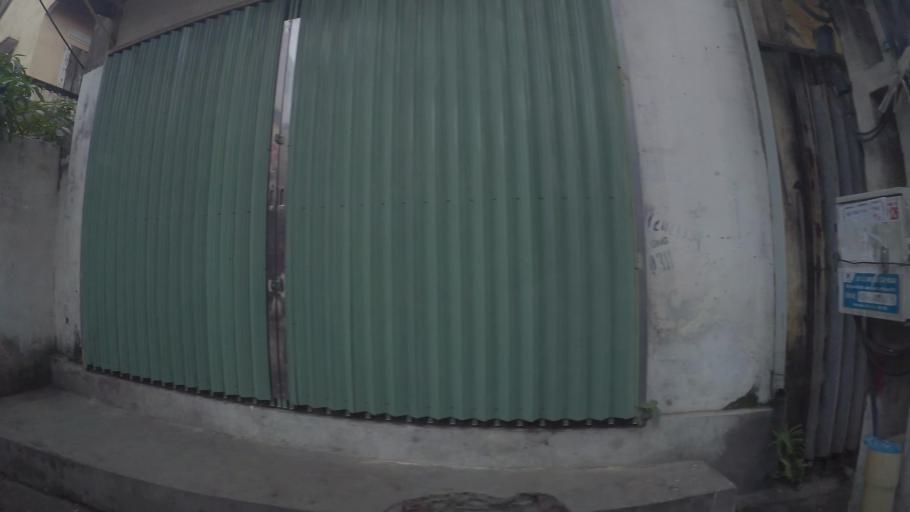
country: VN
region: Ha Noi
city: Van Dien
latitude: 20.9726
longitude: 105.8681
